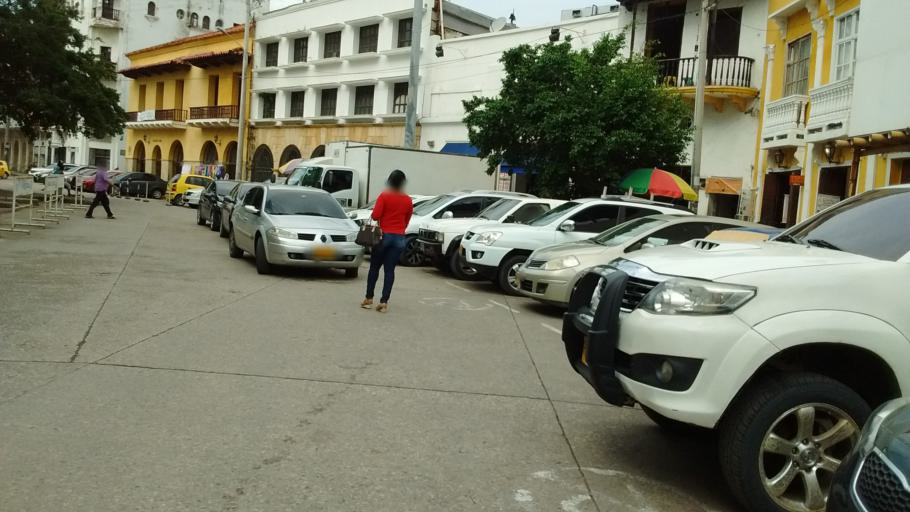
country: CO
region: Bolivar
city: Cartagena
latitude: 10.4246
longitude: -75.5480
